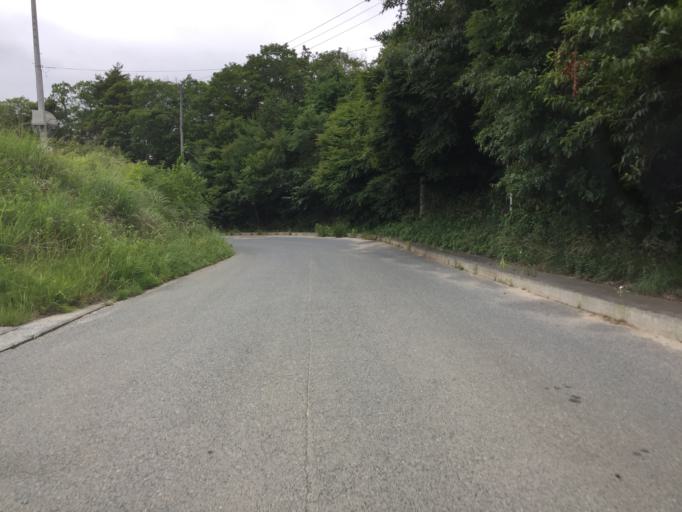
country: JP
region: Miyagi
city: Marumori
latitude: 37.7515
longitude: 140.9640
